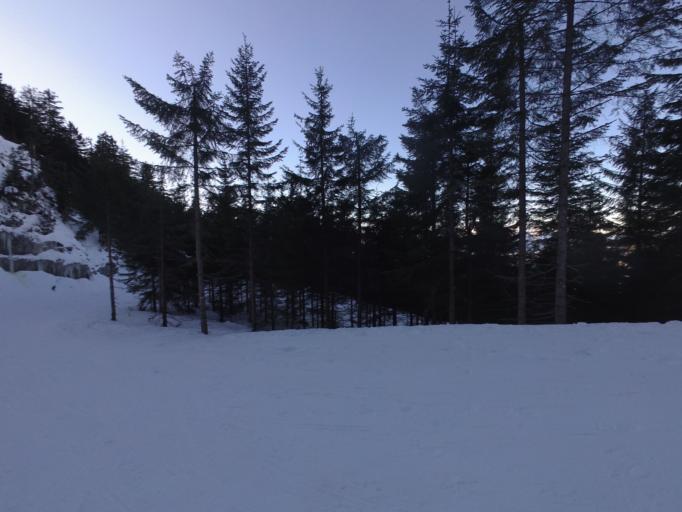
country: AT
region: Salzburg
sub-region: Politischer Bezirk Hallein
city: Scheffau am Tennengebirge
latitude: 47.6378
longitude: 13.2566
